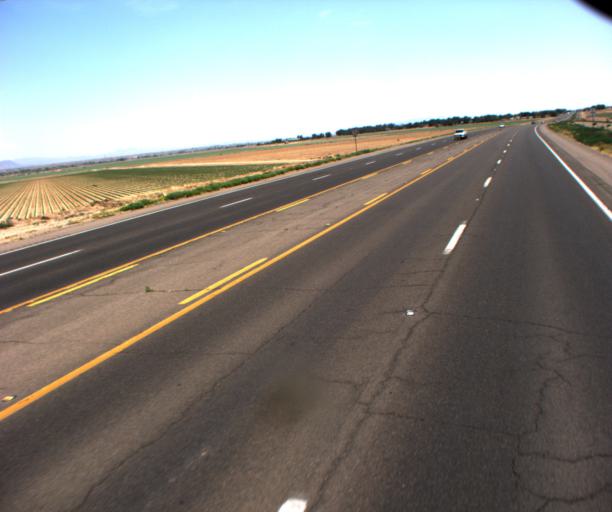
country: US
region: Arizona
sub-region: Graham County
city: Pima
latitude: 32.8827
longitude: -109.8093
